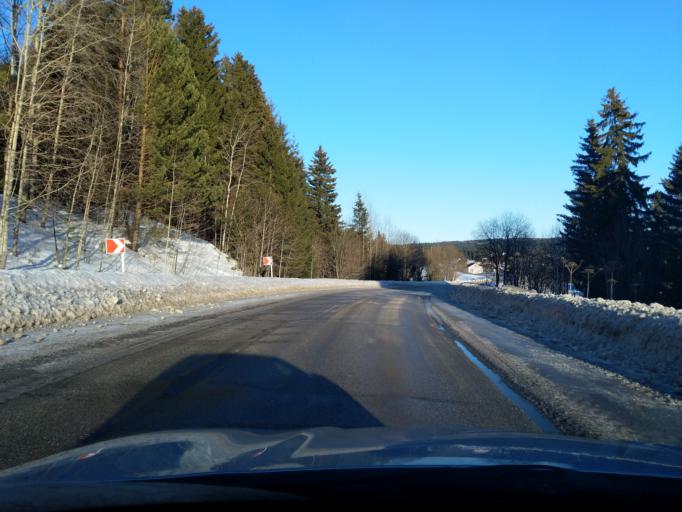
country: RU
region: Perm
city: Polazna
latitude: 58.3058
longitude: 56.4408
